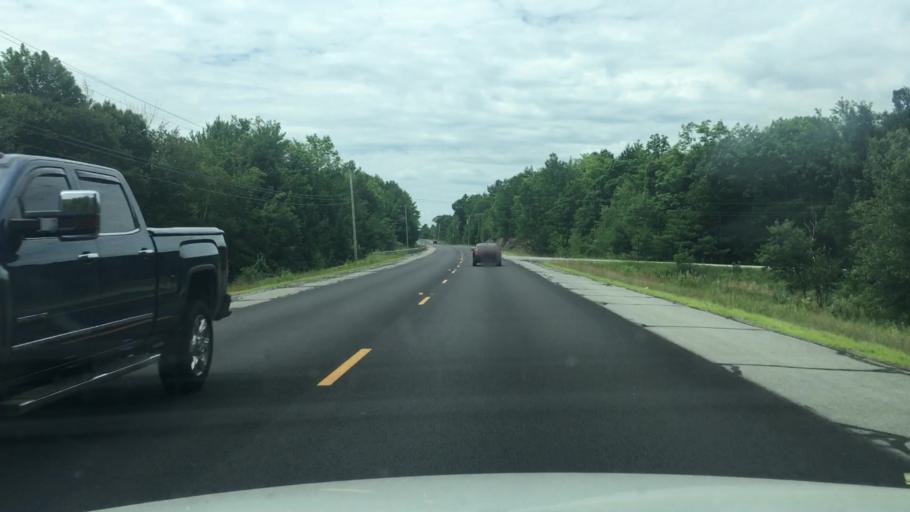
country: US
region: Maine
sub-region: Waldo County
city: Palermo
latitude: 44.4109
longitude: -69.4979
